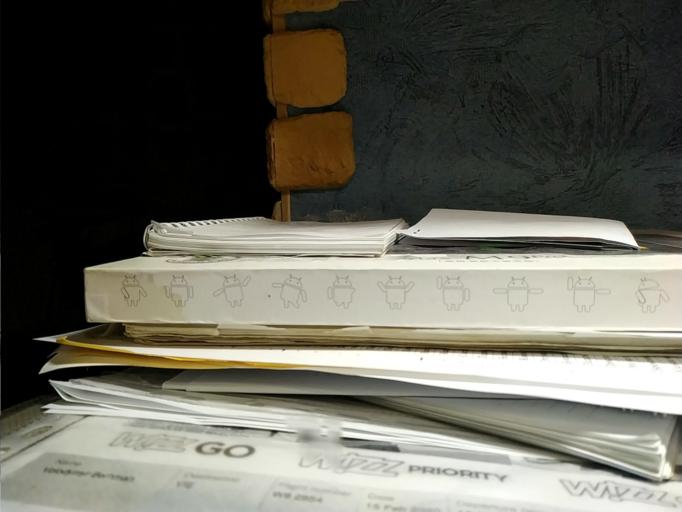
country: RU
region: Arkhangelskaya
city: Konevo
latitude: 62.6870
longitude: 38.6244
